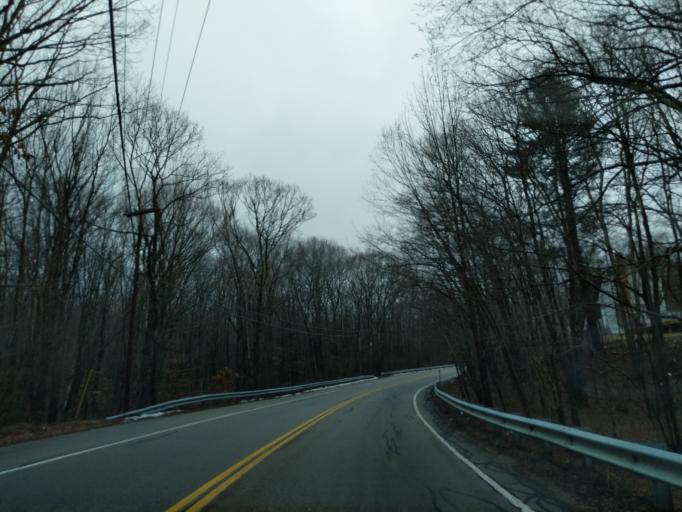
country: US
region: Massachusetts
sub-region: Worcester County
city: Webster
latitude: 42.0567
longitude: -71.8309
